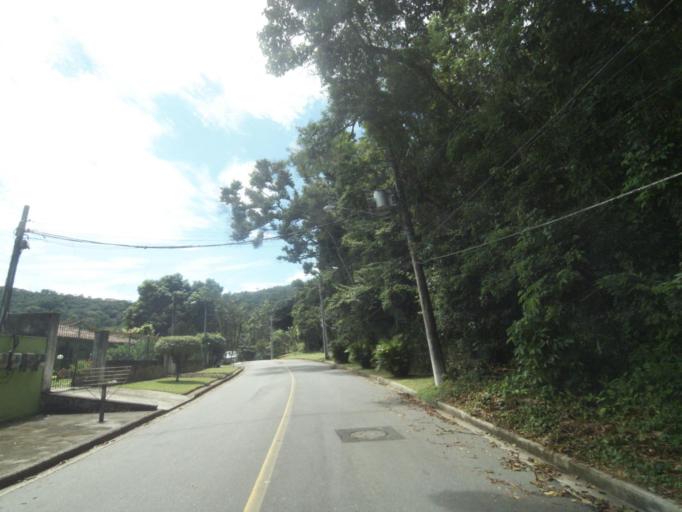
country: BR
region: Rio de Janeiro
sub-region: Niteroi
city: Niteroi
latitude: -22.9547
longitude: -43.0231
